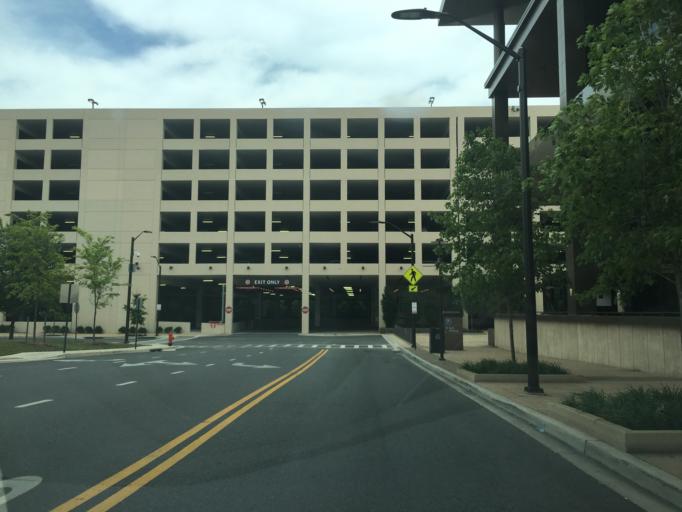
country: US
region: Maryland
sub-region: City of Baltimore
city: Baltimore
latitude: 39.2740
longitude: -76.6268
